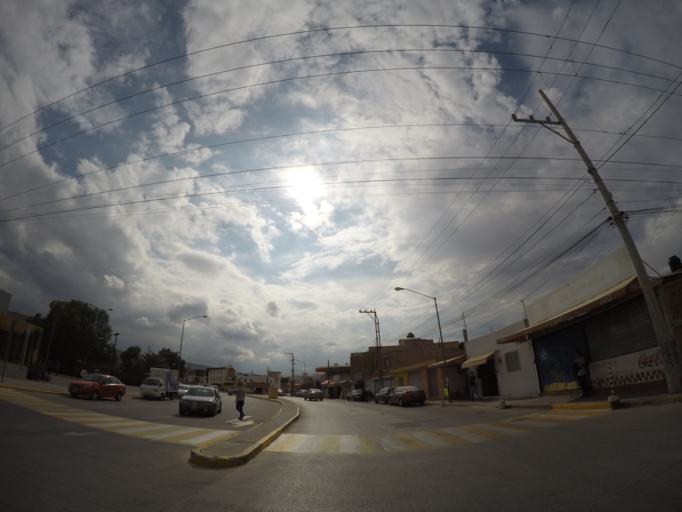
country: MX
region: San Luis Potosi
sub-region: San Luis Potosi
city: San Luis Potosi
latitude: 22.1247
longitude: -100.9837
